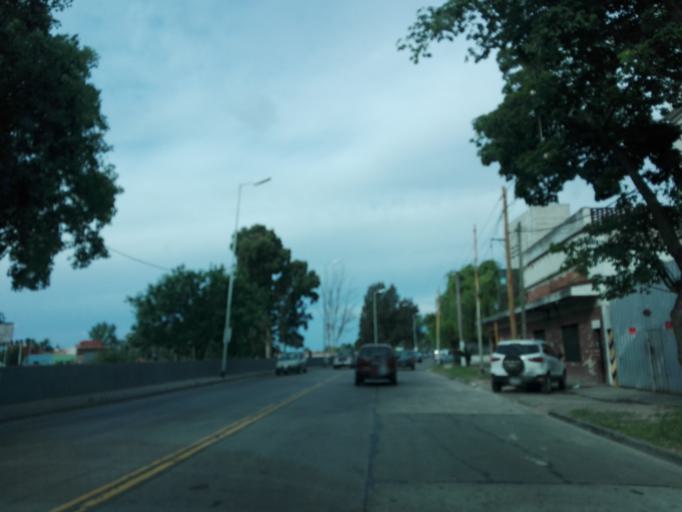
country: AR
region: Buenos Aires
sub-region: Partido de Avellaneda
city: Avellaneda
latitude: -34.6791
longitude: -58.3384
